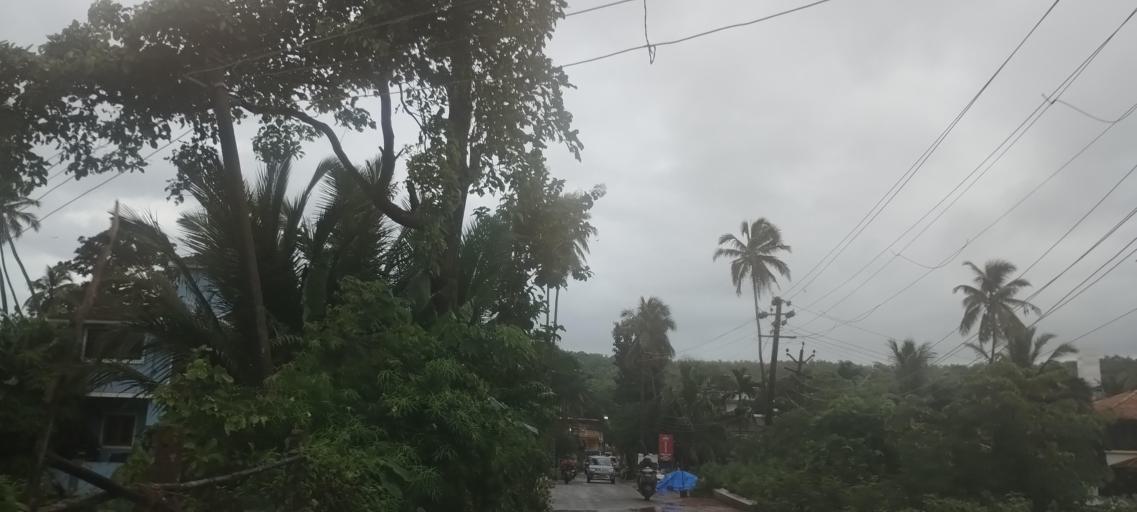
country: IN
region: Goa
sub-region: North Goa
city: Solim
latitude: 15.5967
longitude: 73.7726
